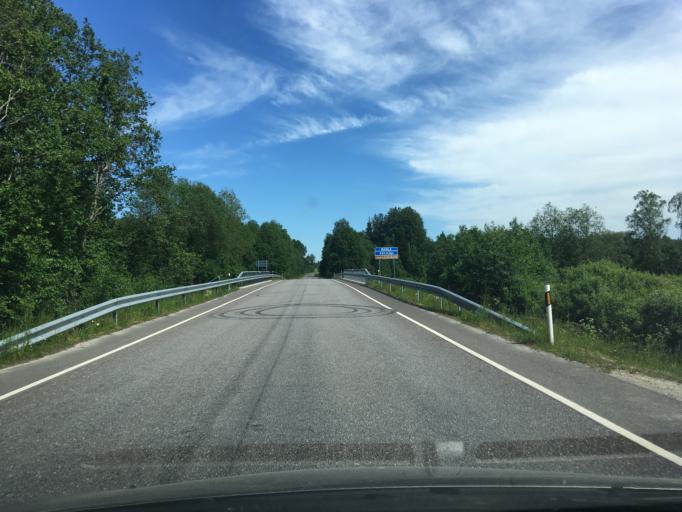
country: EE
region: Raplamaa
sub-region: Rapla vald
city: Rapla
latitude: 59.0503
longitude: 24.8858
